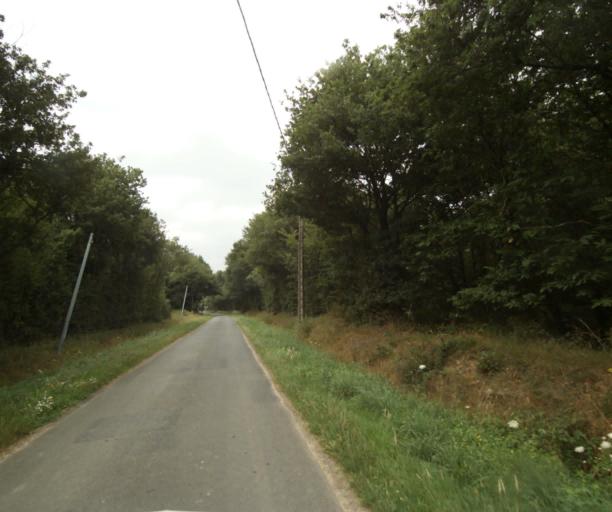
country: FR
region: Pays de la Loire
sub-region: Departement de la Sarthe
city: Juigne-sur-Sarthe
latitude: 47.8379
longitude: -0.2669
